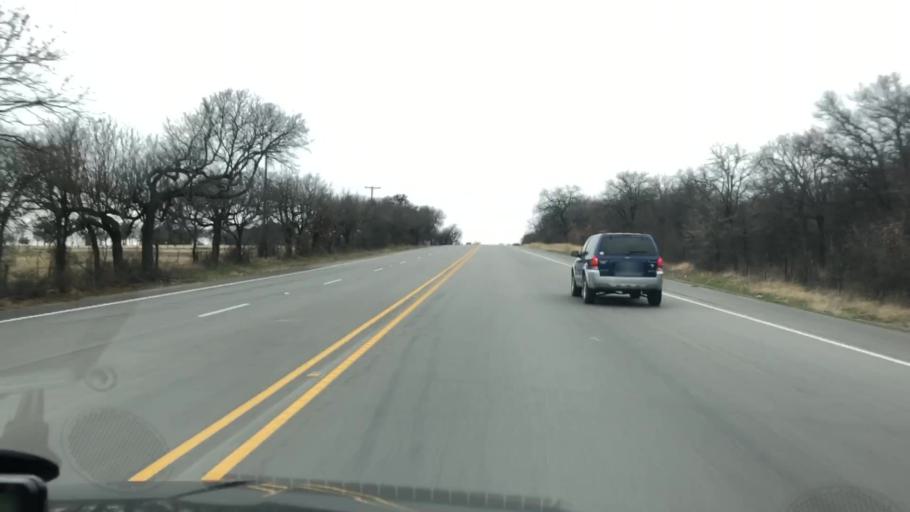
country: US
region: Texas
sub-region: Hamilton County
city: Hico
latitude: 32.0123
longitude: -98.0630
